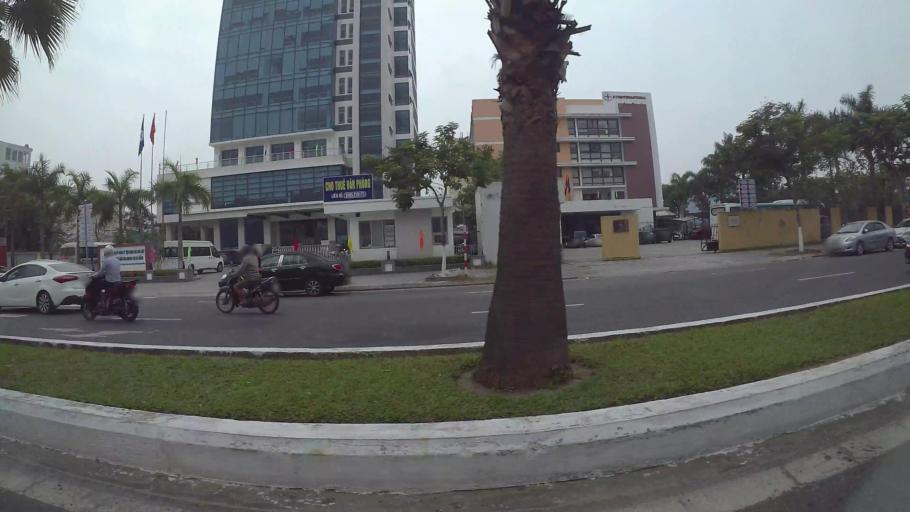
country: VN
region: Da Nang
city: Cam Le
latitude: 16.0317
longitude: 108.2125
